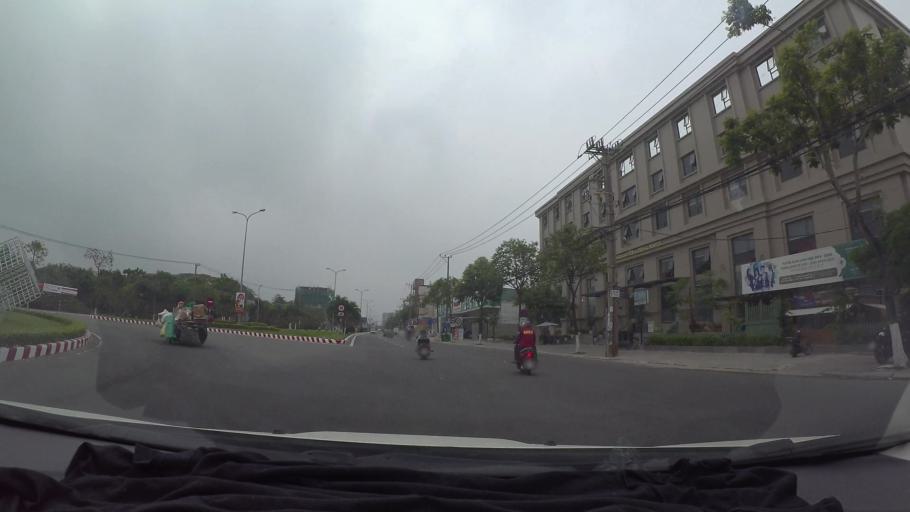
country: VN
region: Da Nang
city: Cam Le
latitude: 16.0313
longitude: 108.2087
